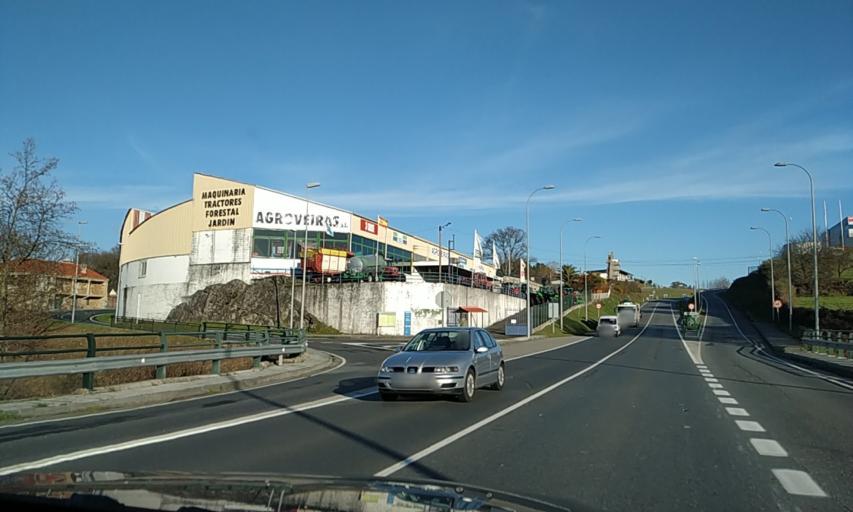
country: ES
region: Galicia
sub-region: Provincia de Pontevedra
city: Silleda
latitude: 42.6943
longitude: -8.2306
